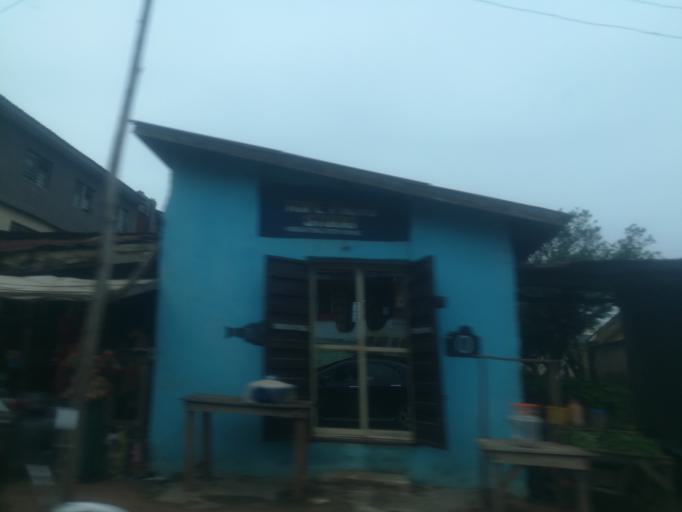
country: NG
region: Oyo
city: Egbeda
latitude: 7.4022
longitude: 3.9791
